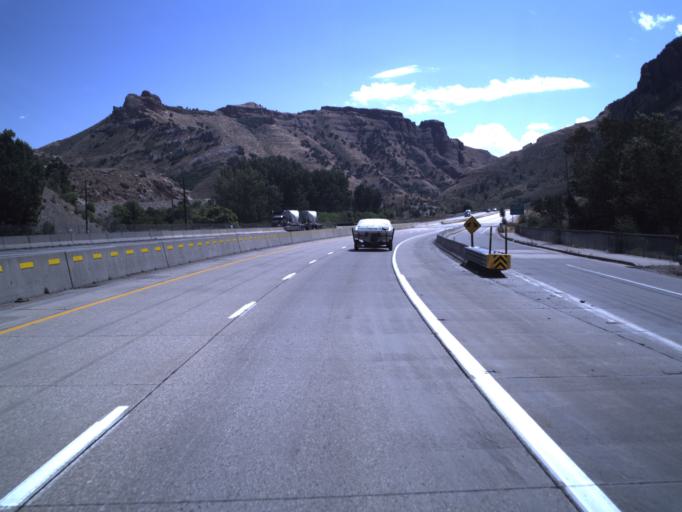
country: US
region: Utah
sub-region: Morgan County
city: Morgan
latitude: 41.0645
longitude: -111.5487
